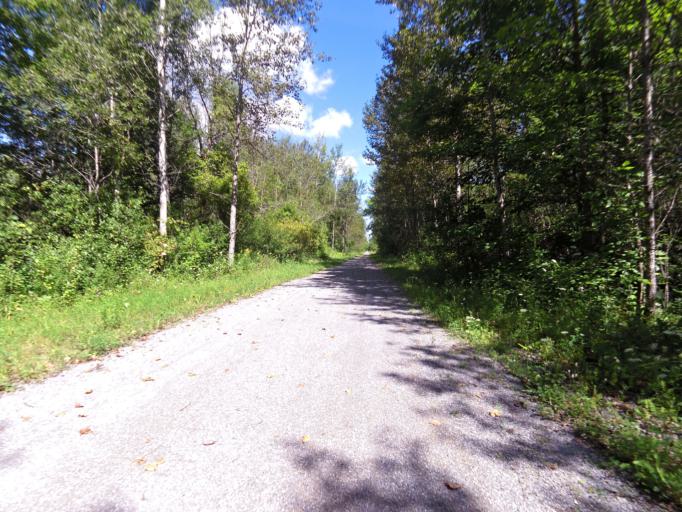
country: CA
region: Ontario
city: Ottawa
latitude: 45.2660
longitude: -75.6235
